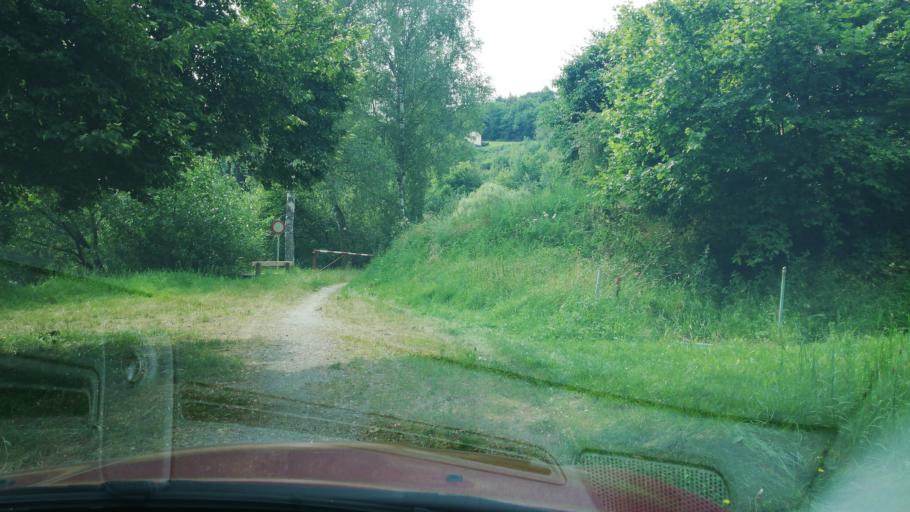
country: AT
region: Upper Austria
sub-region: Politischer Bezirk Rohrbach
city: Kleinzell im Muehlkreis
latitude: 48.4867
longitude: 13.9961
